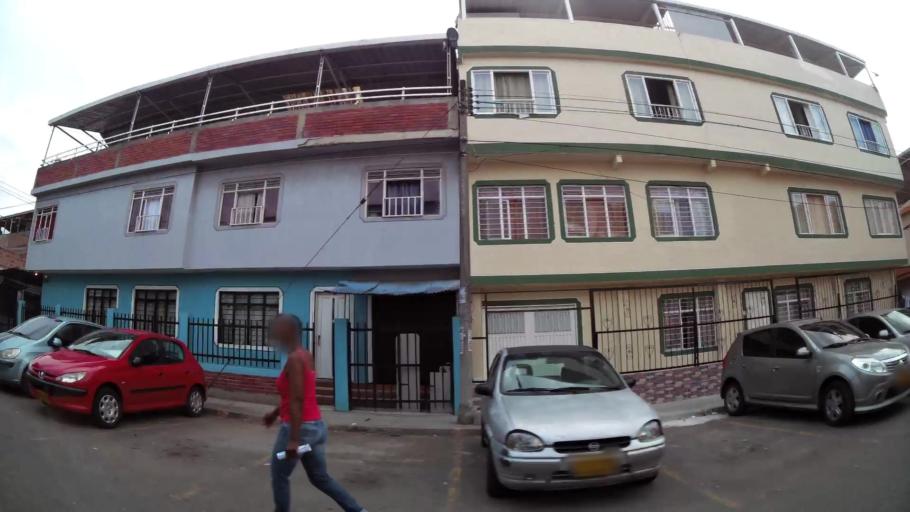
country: CO
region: Valle del Cauca
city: Cali
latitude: 3.4724
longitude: -76.4901
